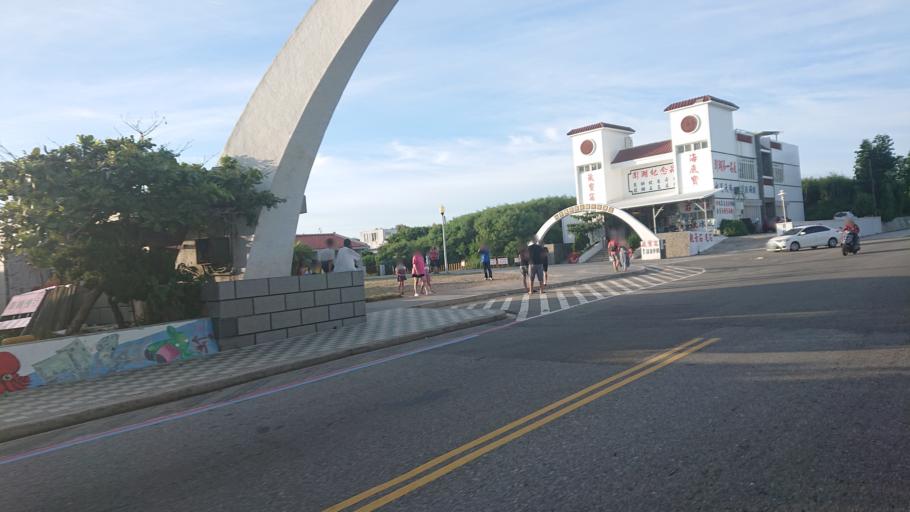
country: TW
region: Taiwan
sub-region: Penghu
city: Ma-kung
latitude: 23.6579
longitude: 119.5546
